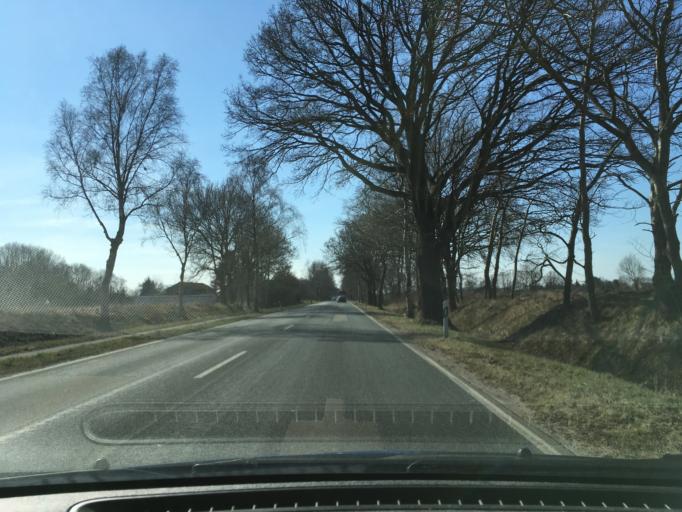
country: DE
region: Lower Saxony
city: Ottersberg
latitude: 53.0760
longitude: 9.1026
